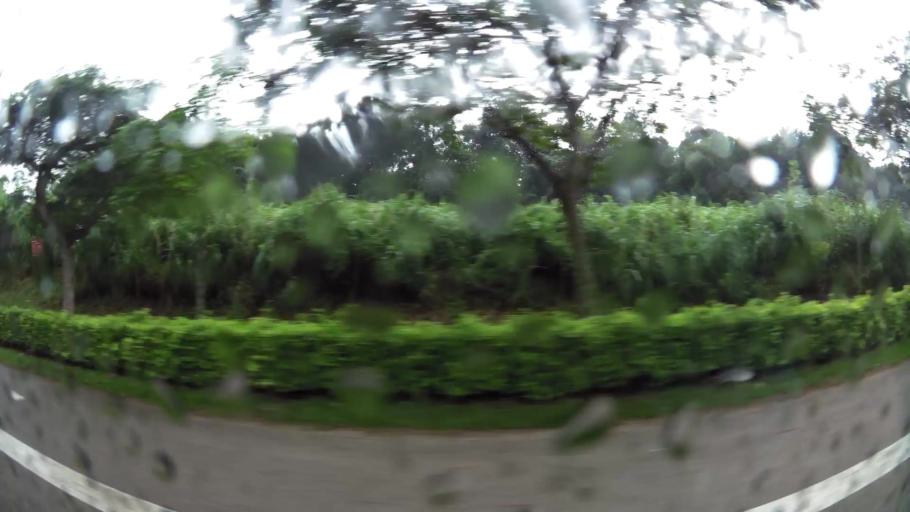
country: MY
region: Johor
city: Kampung Pasir Gudang Baru
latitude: 1.3928
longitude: 103.8282
